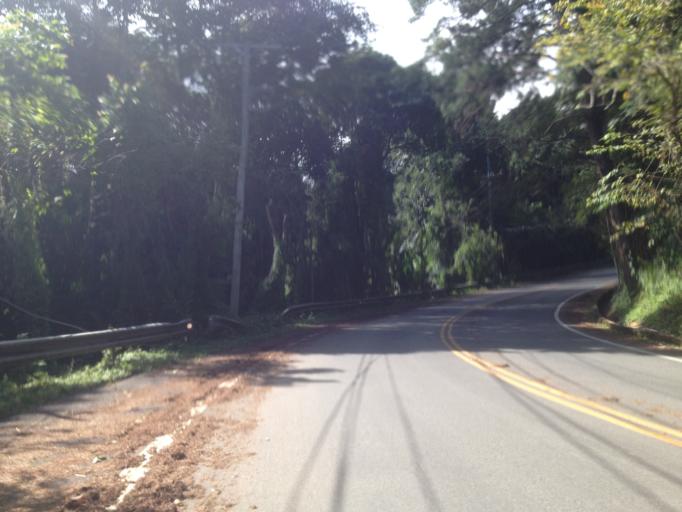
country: TH
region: Chiang Mai
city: Chiang Mai
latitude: 18.8064
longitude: 98.9144
